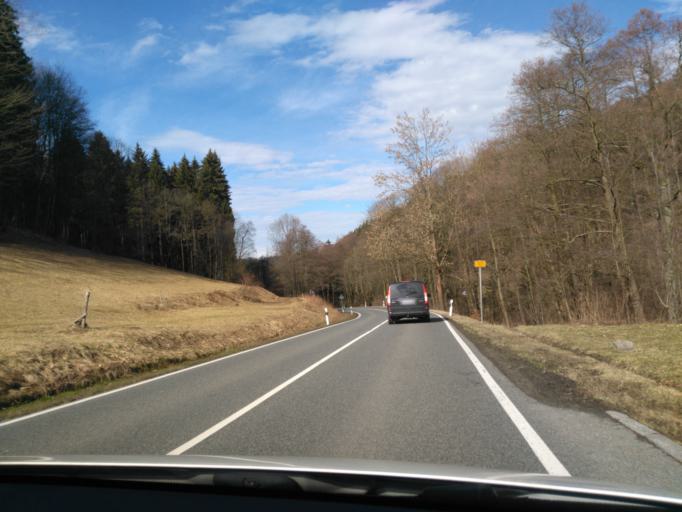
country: DE
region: Saxony
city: Wolkenstein
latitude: 50.6634
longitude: 13.0735
